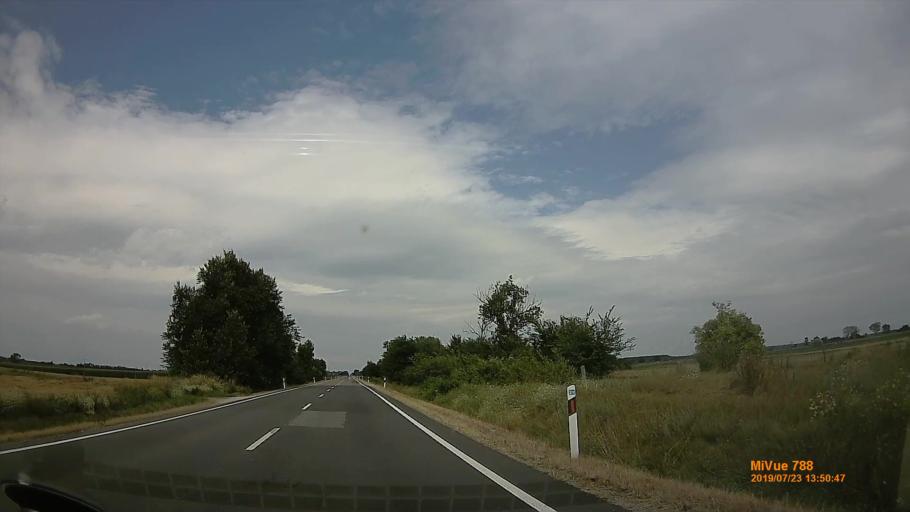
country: HU
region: Hajdu-Bihar
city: Polgar
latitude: 47.8792
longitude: 21.1456
